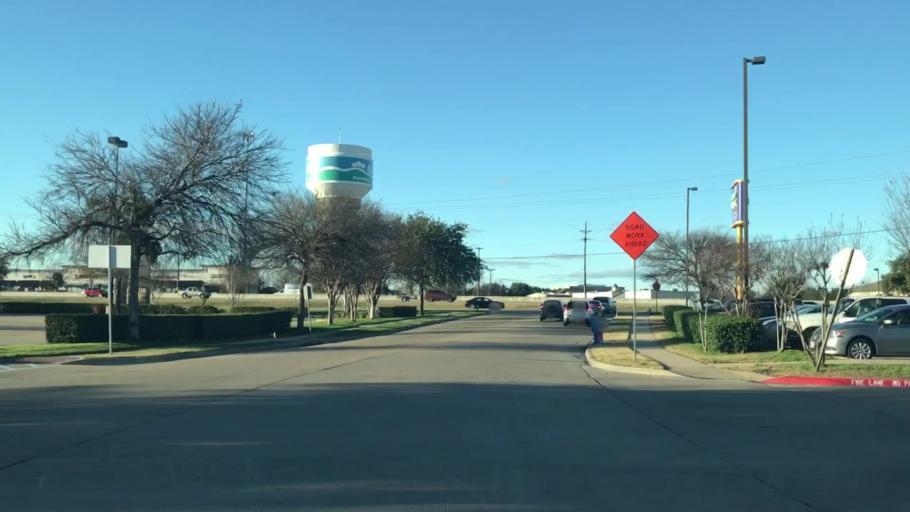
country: US
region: Texas
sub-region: Rockwall County
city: Rockwall
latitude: 32.8978
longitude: -96.4632
